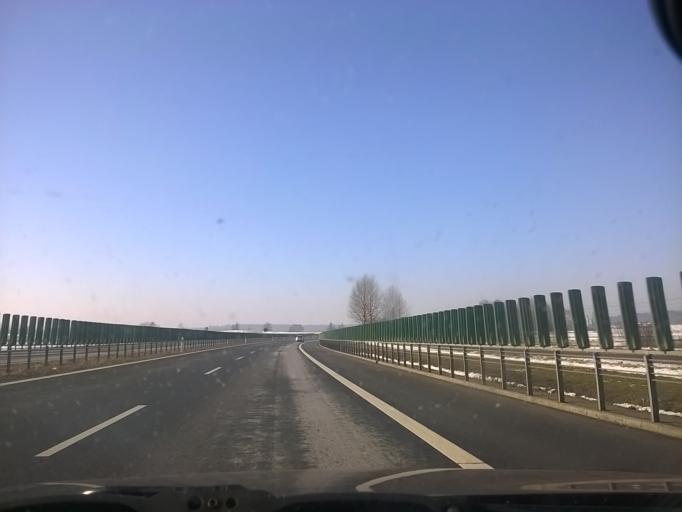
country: PL
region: Warmian-Masurian Voivodeship
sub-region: Powiat olsztynski
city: Biskupiec
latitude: 53.8354
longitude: 21.0283
